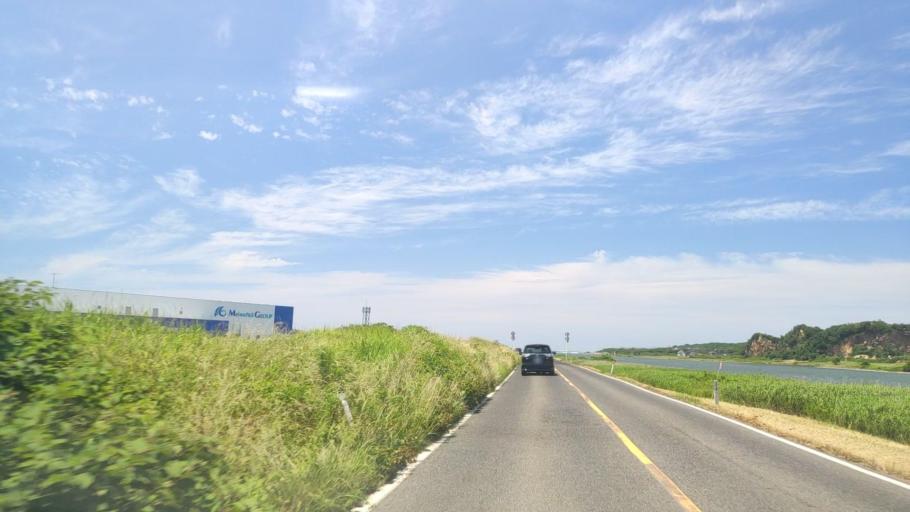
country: JP
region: Tottori
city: Tottori
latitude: 35.5233
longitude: 134.2061
